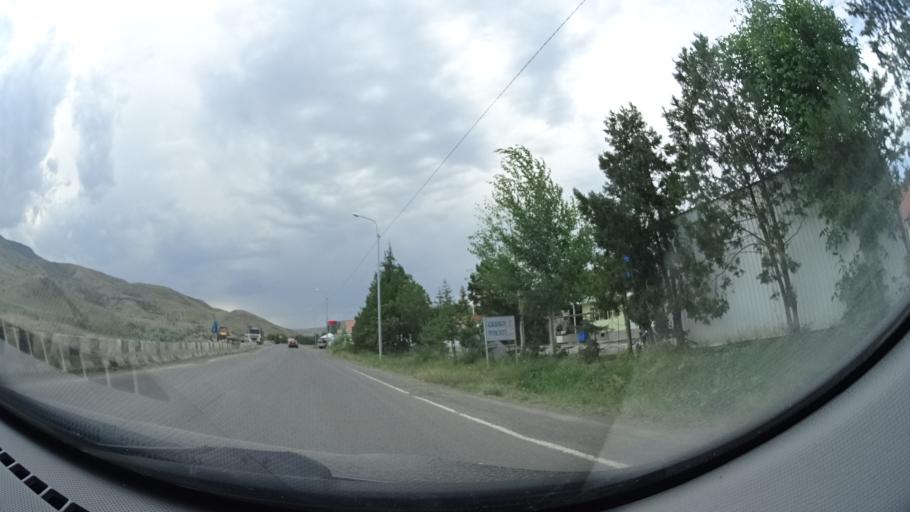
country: GE
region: Samtskhe-Javakheti
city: Aspindza
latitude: 41.5865
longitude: 43.2410
